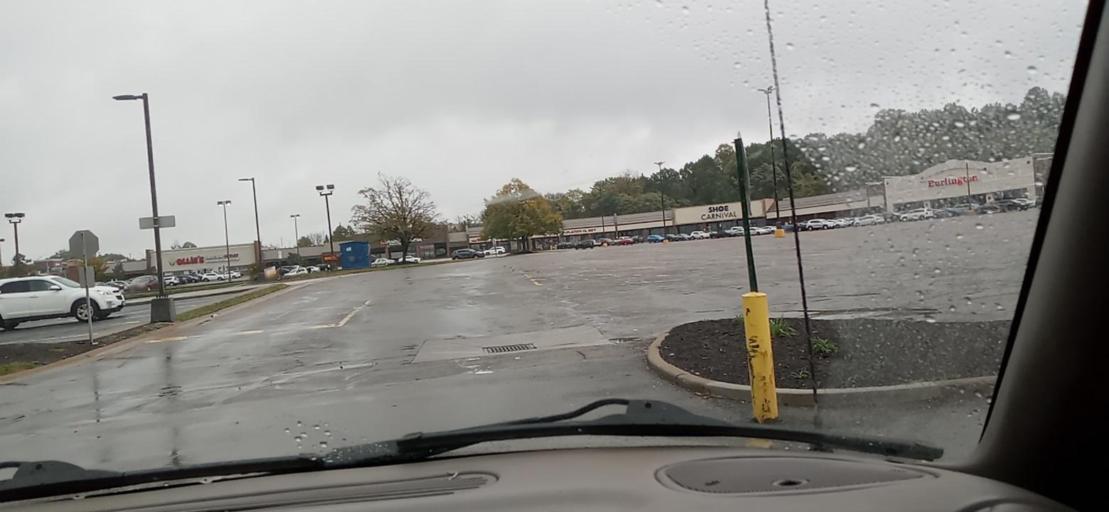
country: US
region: Ohio
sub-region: Summit County
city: Cuyahoga Falls
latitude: 41.1180
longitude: -81.4776
